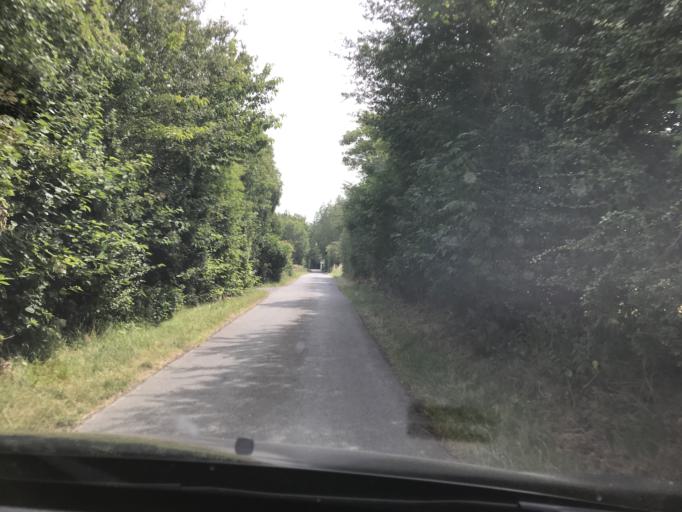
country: DK
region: South Denmark
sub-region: AEro Kommune
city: AEroskobing
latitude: 54.9154
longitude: 10.2629
